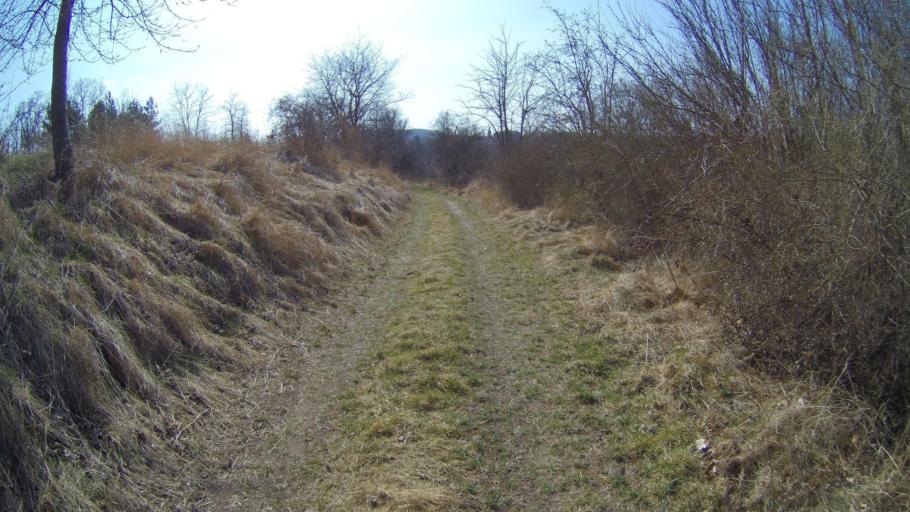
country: CZ
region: Ustecky
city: Mecholupy
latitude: 50.2861
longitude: 13.5658
